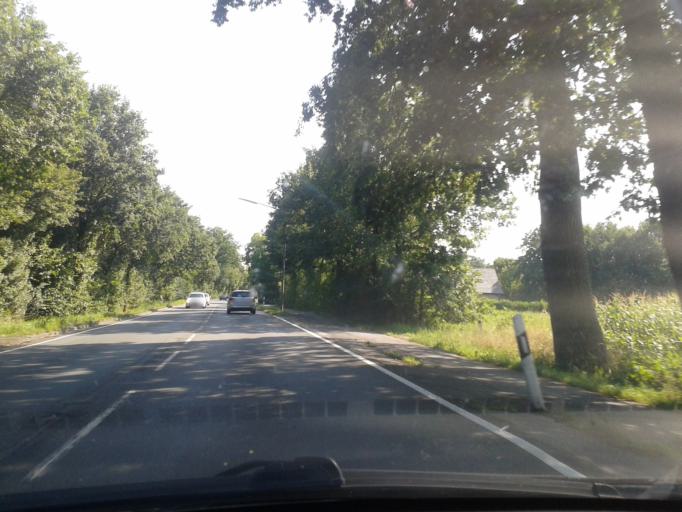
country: DE
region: North Rhine-Westphalia
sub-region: Regierungsbezirk Detmold
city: Delbruck
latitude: 51.7346
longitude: 8.5581
